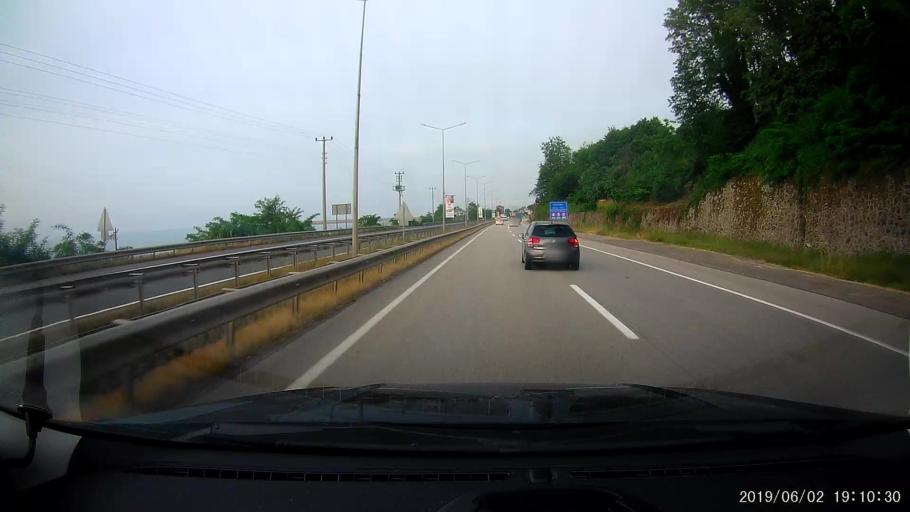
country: TR
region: Ordu
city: Gulyali
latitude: 40.9686
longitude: 38.0457
